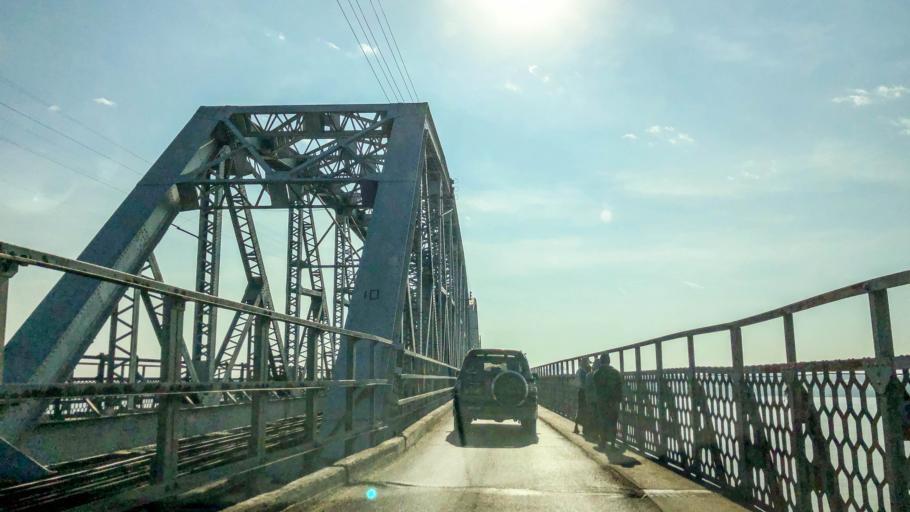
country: MM
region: Sagain
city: Sagaing
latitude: 21.8747
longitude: 95.9882
